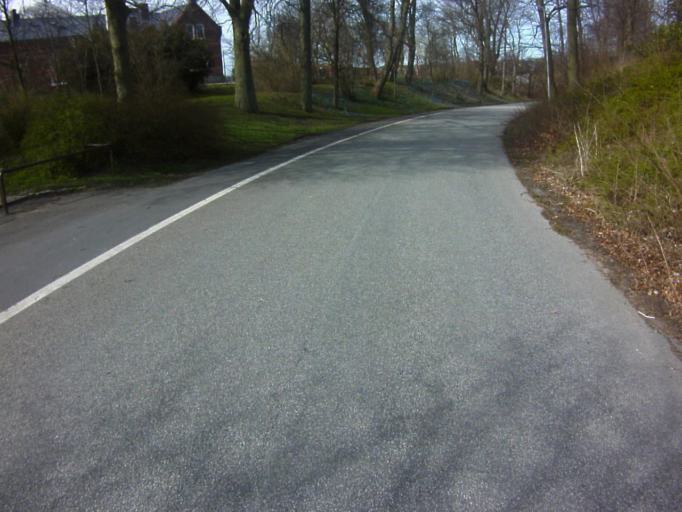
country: SE
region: Skane
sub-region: Kavlinge Kommun
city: Kaevlinge
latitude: 55.7746
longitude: 13.1109
